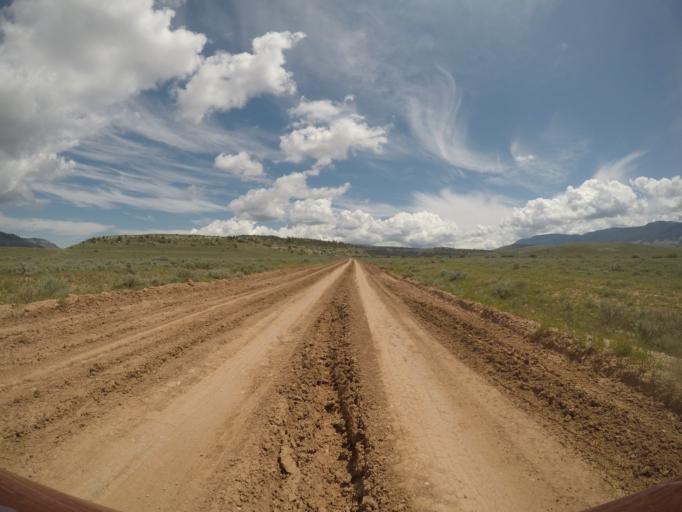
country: US
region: Montana
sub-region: Yellowstone County
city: Laurel
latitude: 45.2436
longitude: -108.6592
